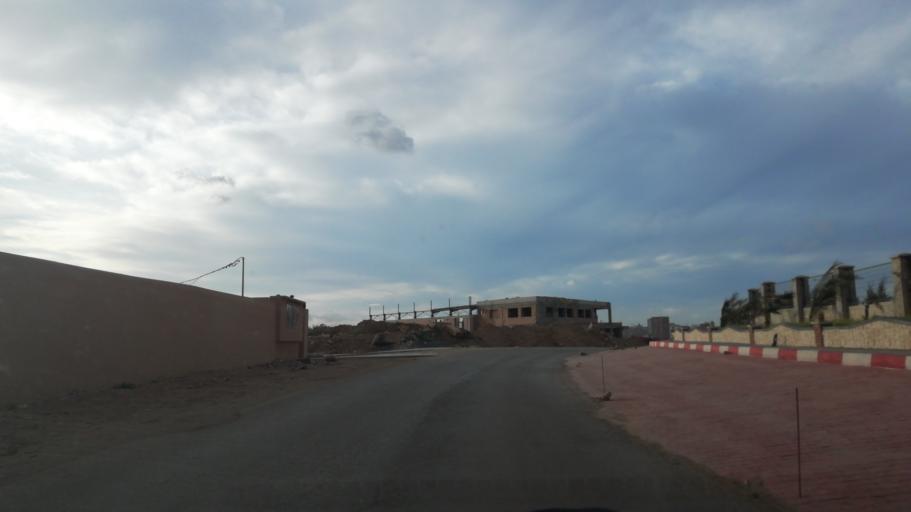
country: DZ
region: Oran
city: Bir el Djir
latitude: 35.7151
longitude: -0.5572
